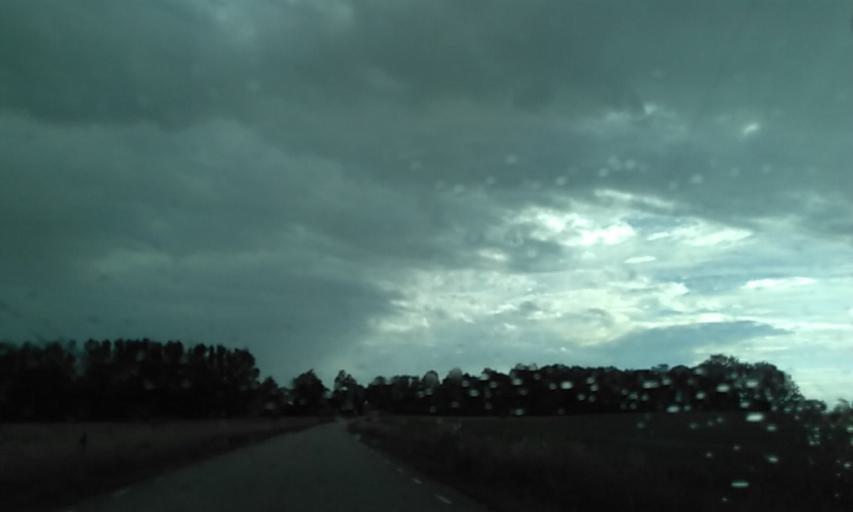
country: SE
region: Vaestra Goetaland
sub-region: Grastorps Kommun
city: Graestorp
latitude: 58.4335
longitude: 12.7429
